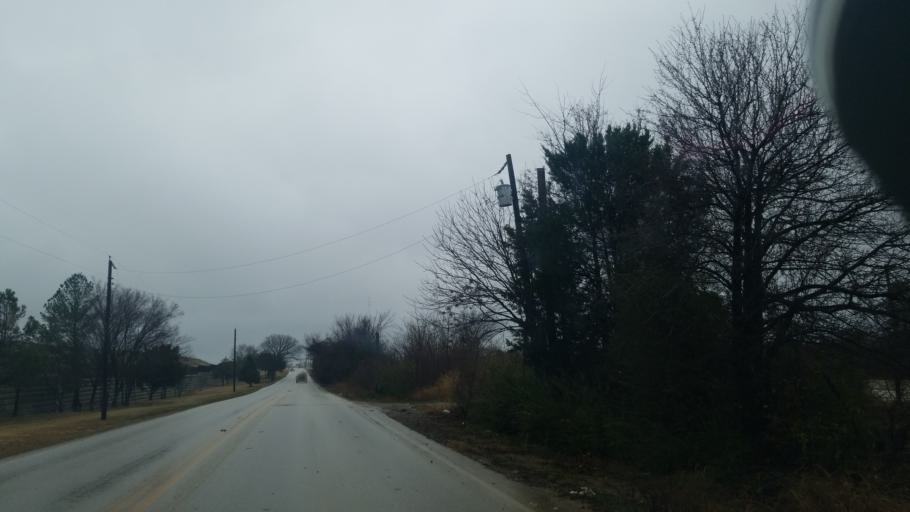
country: US
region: Texas
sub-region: Denton County
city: Corinth
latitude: 33.1911
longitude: -97.0851
